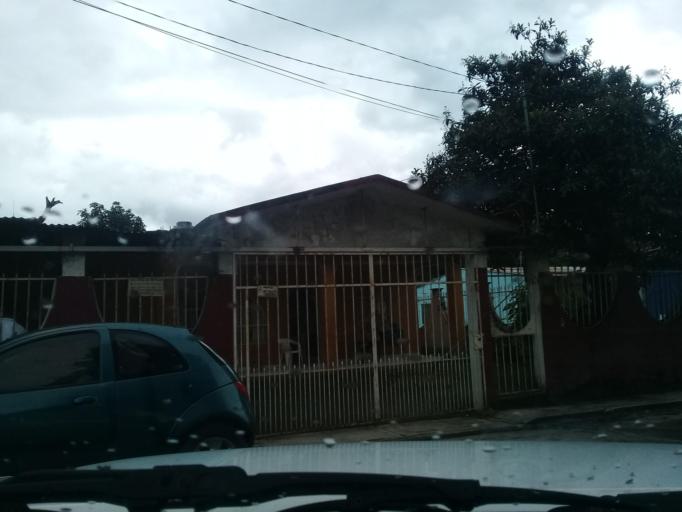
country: MX
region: Veracruz
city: San Andres Tuxtla
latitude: 18.4420
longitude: -95.2075
